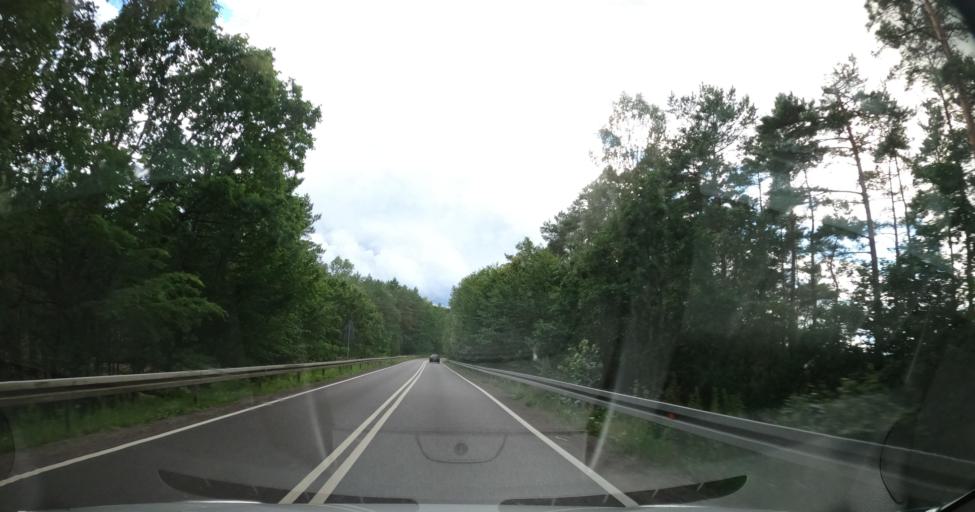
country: PL
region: Pomeranian Voivodeship
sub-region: Powiat bytowski
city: Czarna Dabrowka
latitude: 54.3393
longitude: 17.6324
